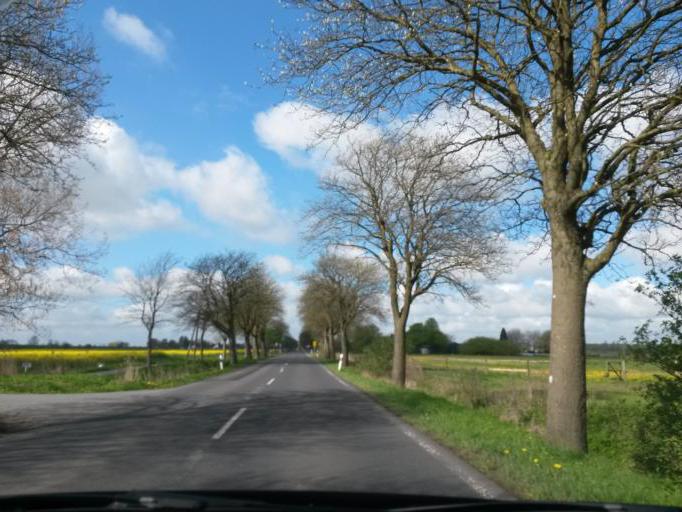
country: DE
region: Schleswig-Holstein
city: Holm
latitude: 53.6133
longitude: 9.6531
